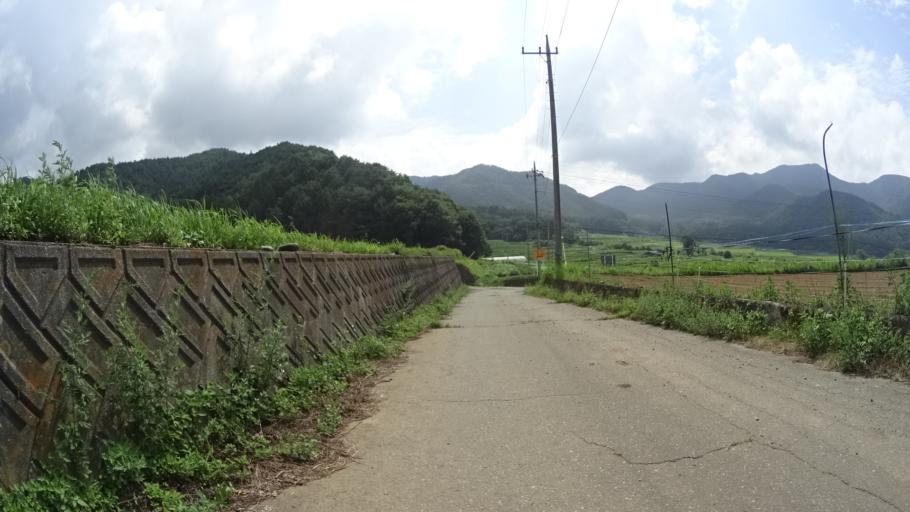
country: JP
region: Yamanashi
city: Nirasaki
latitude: 35.8939
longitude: 138.4699
